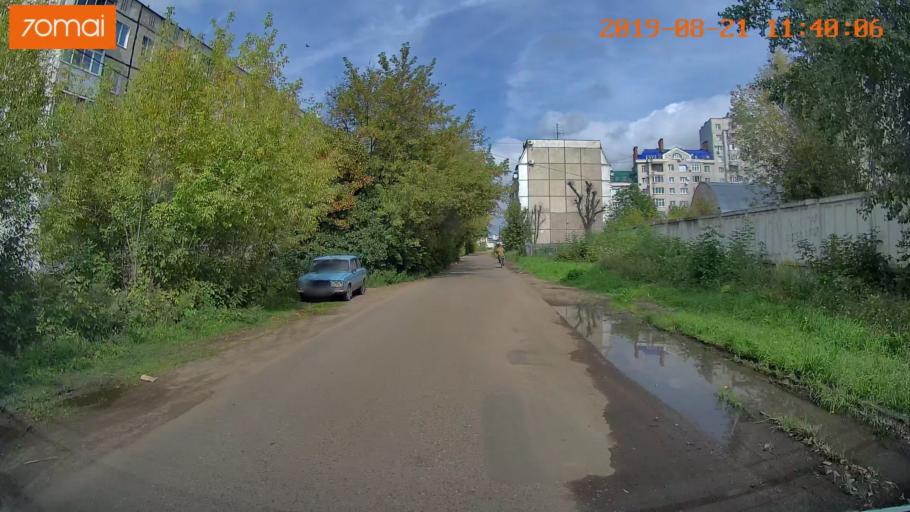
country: RU
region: Ivanovo
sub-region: Gorod Ivanovo
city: Ivanovo
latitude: 57.0016
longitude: 40.9377
